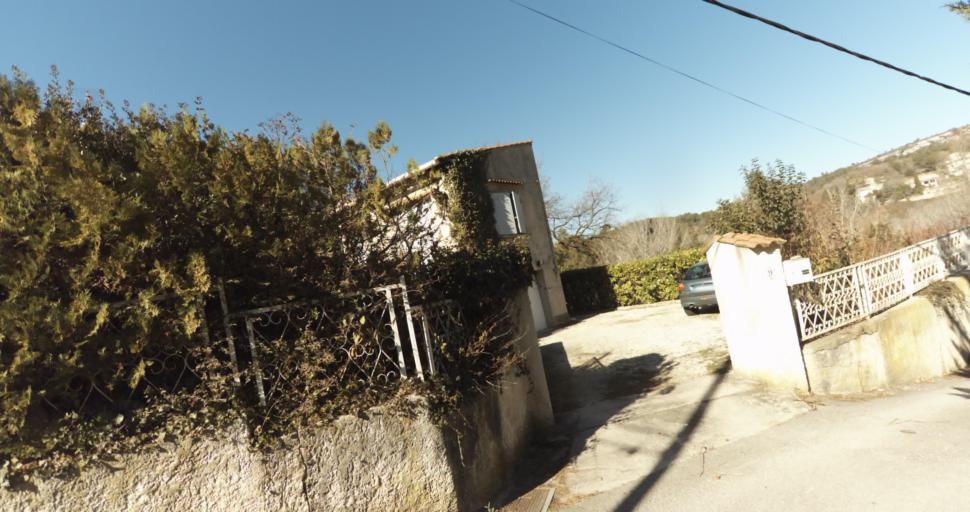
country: FR
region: Provence-Alpes-Cote d'Azur
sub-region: Departement des Bouches-du-Rhone
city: La Bouilladisse
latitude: 43.3924
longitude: 5.5864
